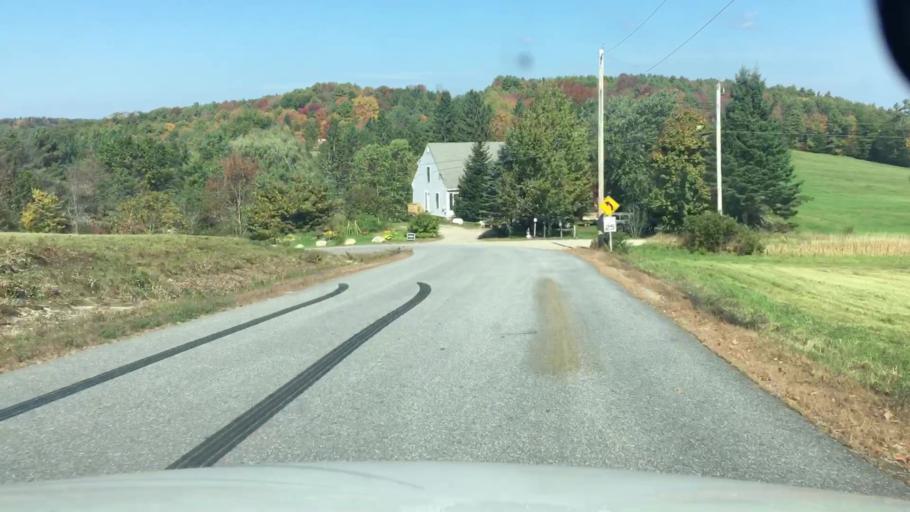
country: US
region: Maine
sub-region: Sagadahoc County
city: Topsham
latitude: 44.0118
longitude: -69.9615
